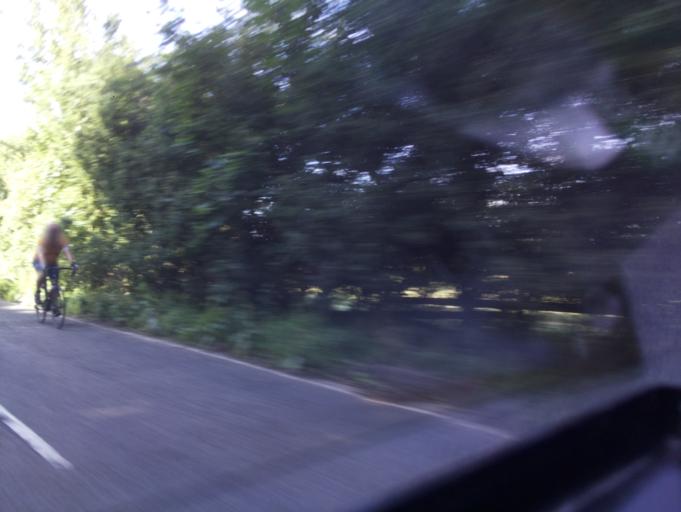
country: GB
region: England
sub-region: South Gloucestershire
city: Pucklechurch
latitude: 51.4465
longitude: -2.4175
